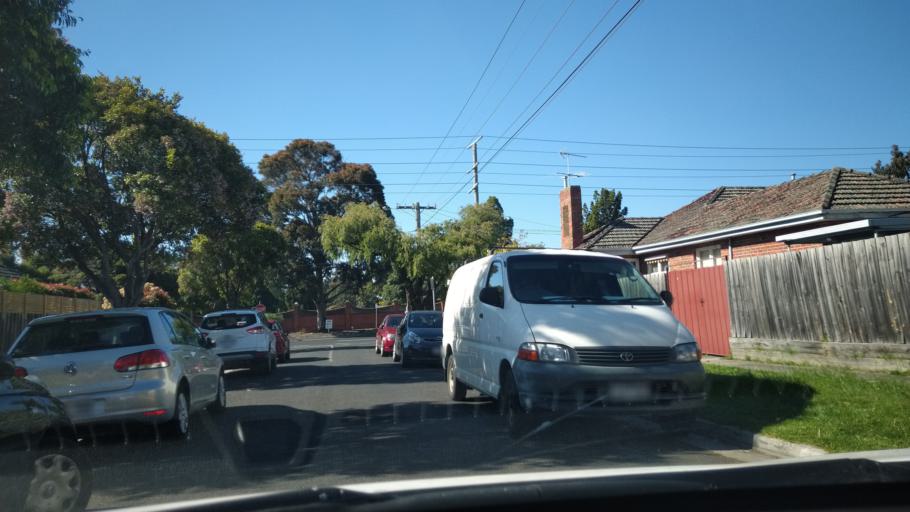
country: AU
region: Victoria
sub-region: Bayside
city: Brighton East
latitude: -37.9020
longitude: 145.0202
